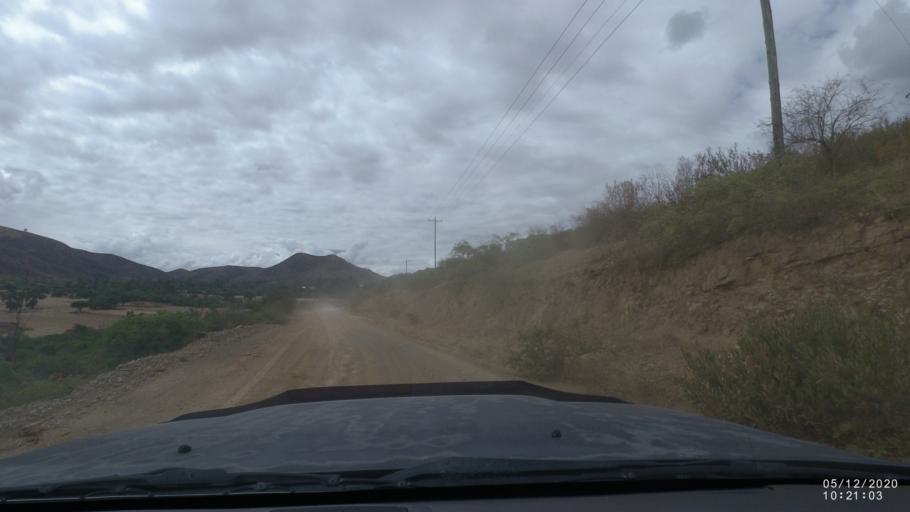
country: BO
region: Cochabamba
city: Sipe Sipe
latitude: -17.4871
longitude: -66.2827
